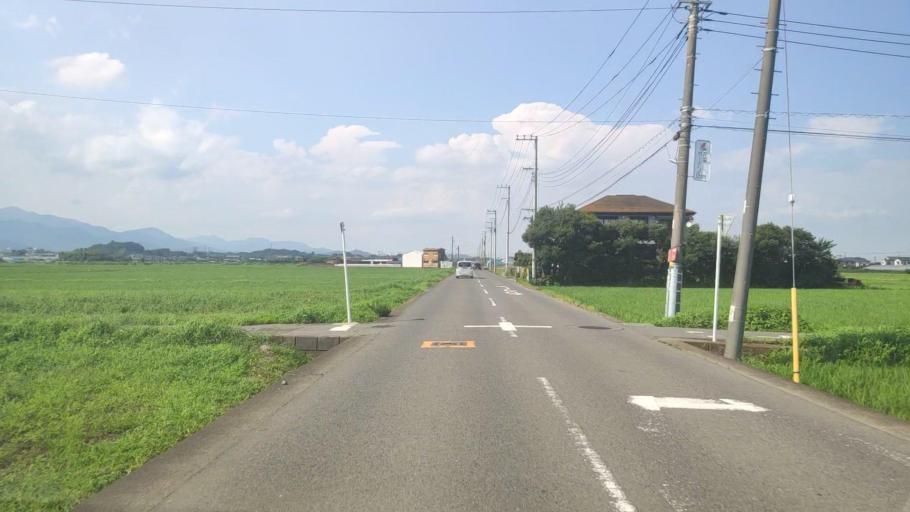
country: JP
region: Kanagawa
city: Isehara
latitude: 35.3584
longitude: 139.3159
